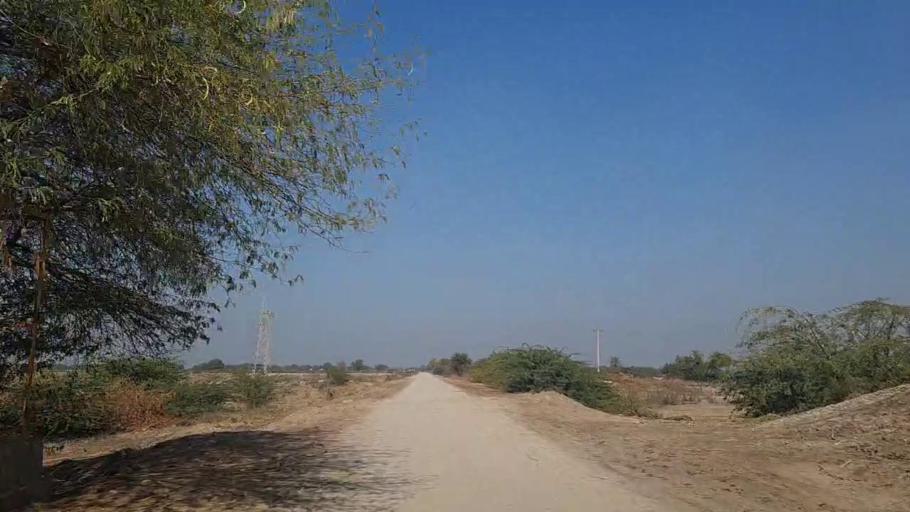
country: PK
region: Sindh
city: Nawabshah
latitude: 26.2194
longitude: 68.3378
